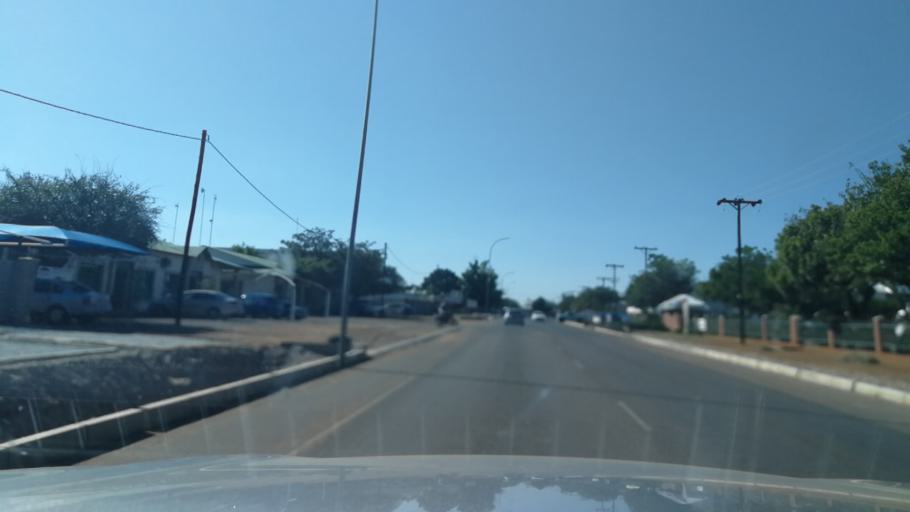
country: BW
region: South East
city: Gaborone
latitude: -24.6954
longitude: 25.8834
